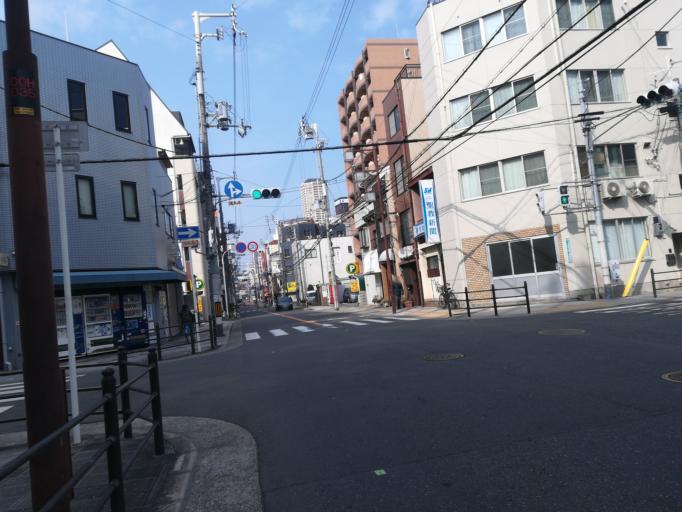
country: JP
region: Osaka
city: Osaka-shi
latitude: 34.6584
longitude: 135.5084
